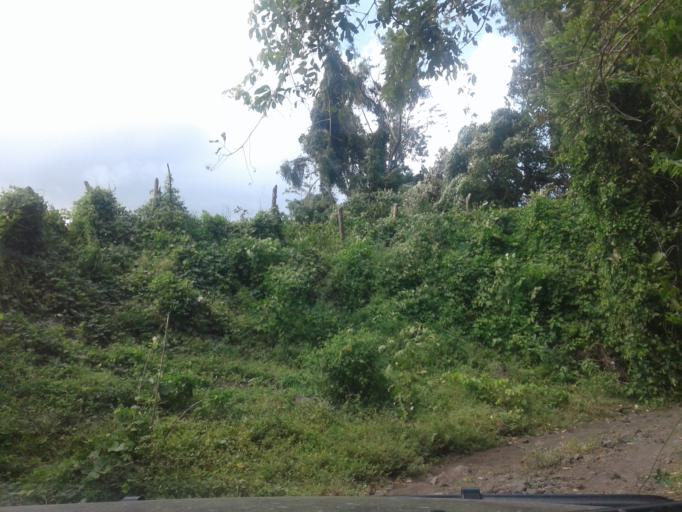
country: NI
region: Rivas
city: Moyogalpa
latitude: 11.5516
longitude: -85.6597
